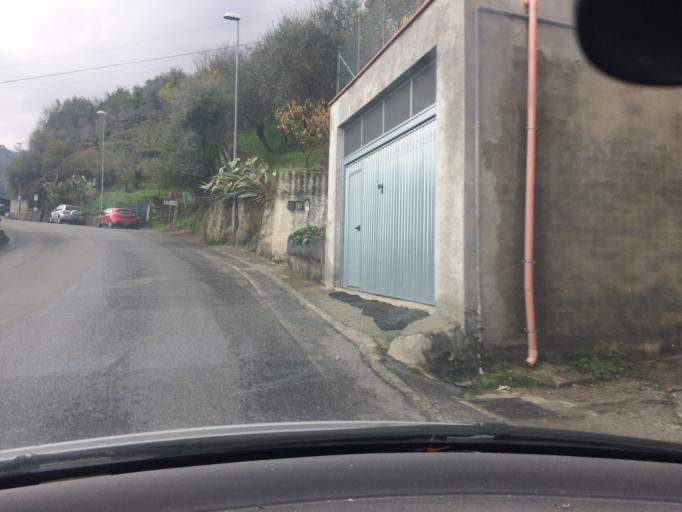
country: IT
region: Tuscany
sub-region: Provincia di Massa-Carrara
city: Massa
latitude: 44.0505
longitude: 10.1288
